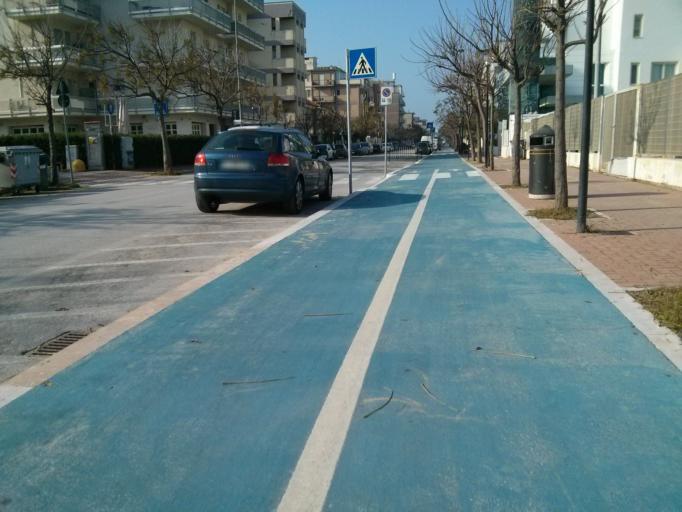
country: IT
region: The Marches
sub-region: Provincia di Pesaro e Urbino
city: Pesaro
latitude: 43.9068
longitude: 12.9278
